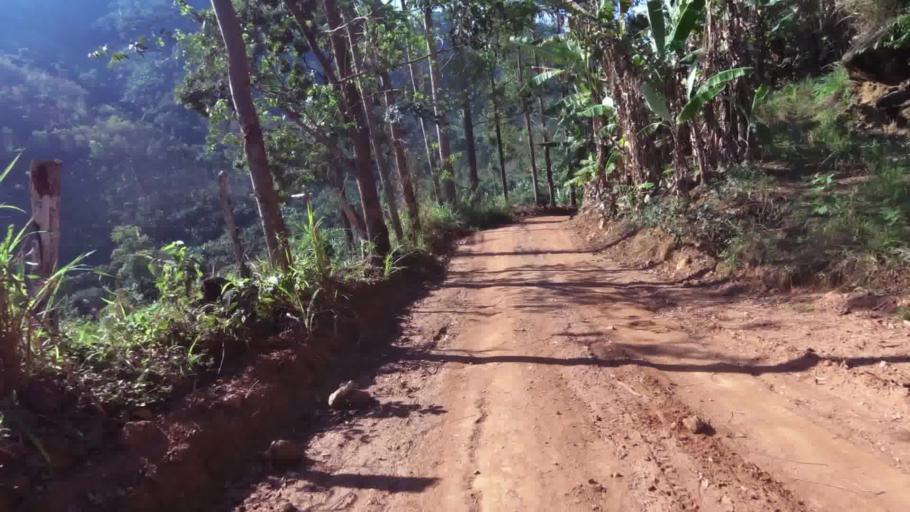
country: BR
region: Espirito Santo
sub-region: Alfredo Chaves
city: Alfredo Chaves
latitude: -20.6037
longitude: -40.7628
